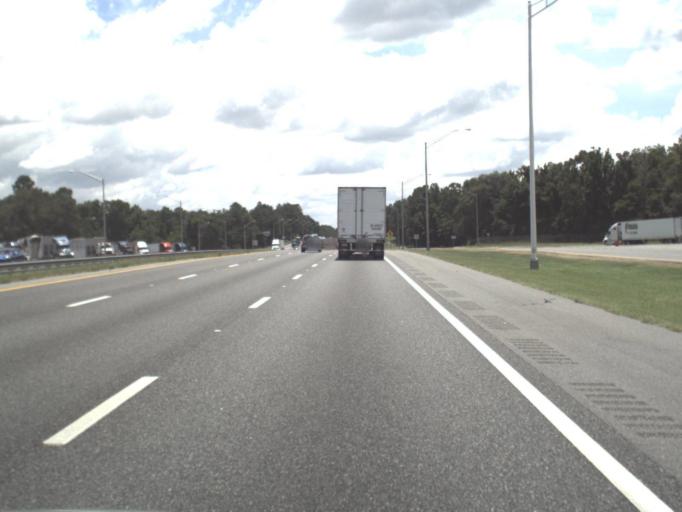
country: US
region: Florida
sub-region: Alachua County
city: High Springs
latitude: 29.9789
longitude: -82.5790
